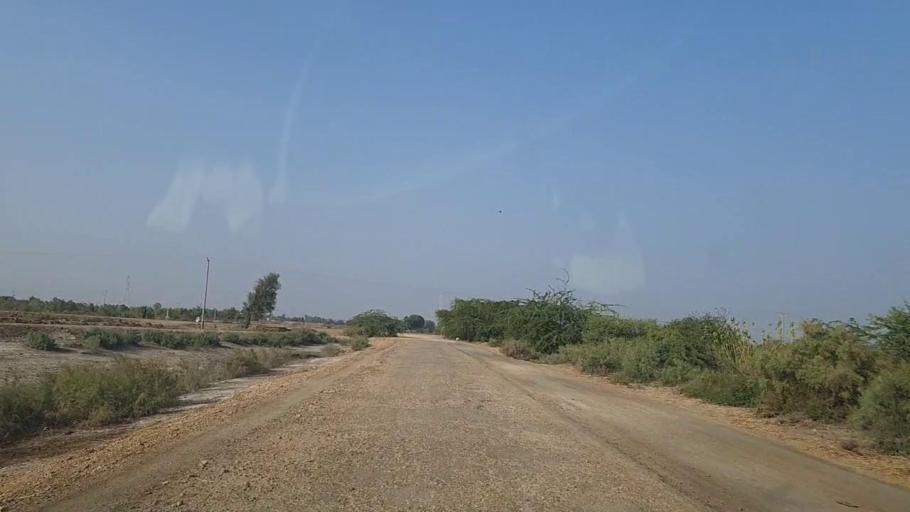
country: PK
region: Sindh
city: Mirpur Sakro
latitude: 24.5593
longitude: 67.6711
